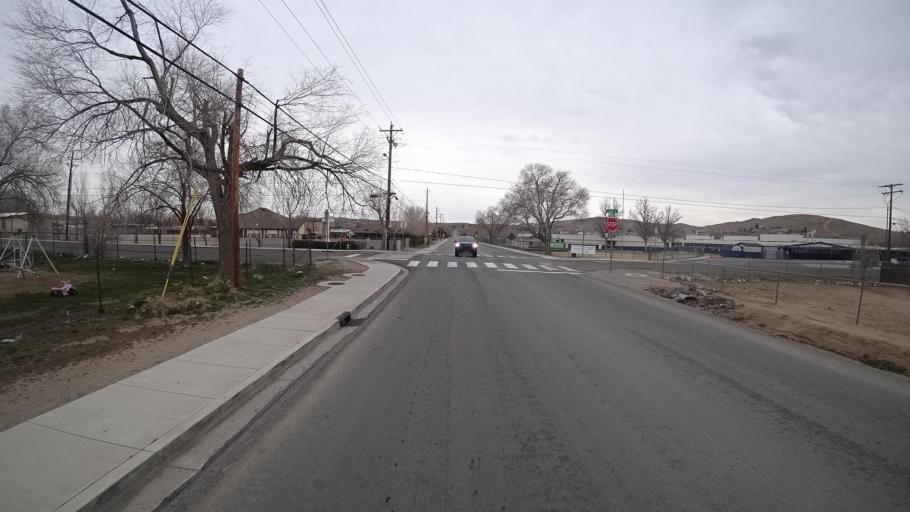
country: US
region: Nevada
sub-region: Washoe County
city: Sun Valley
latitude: 39.5928
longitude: -119.7761
